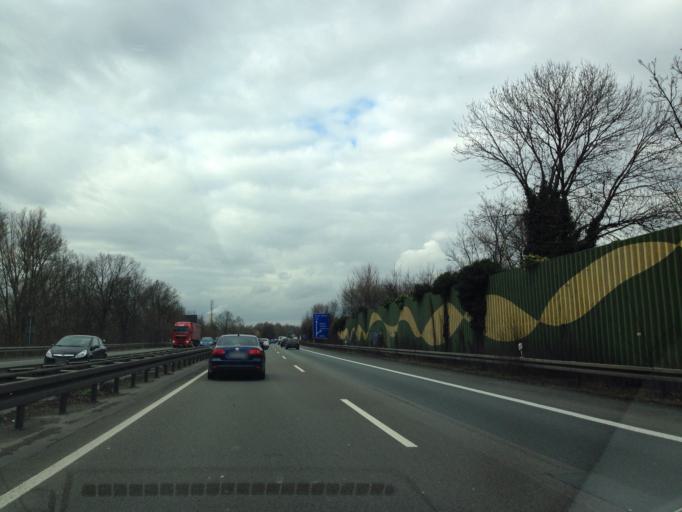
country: DE
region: North Rhine-Westphalia
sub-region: Regierungsbezirk Arnsberg
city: Herne
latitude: 51.5225
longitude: 7.2096
